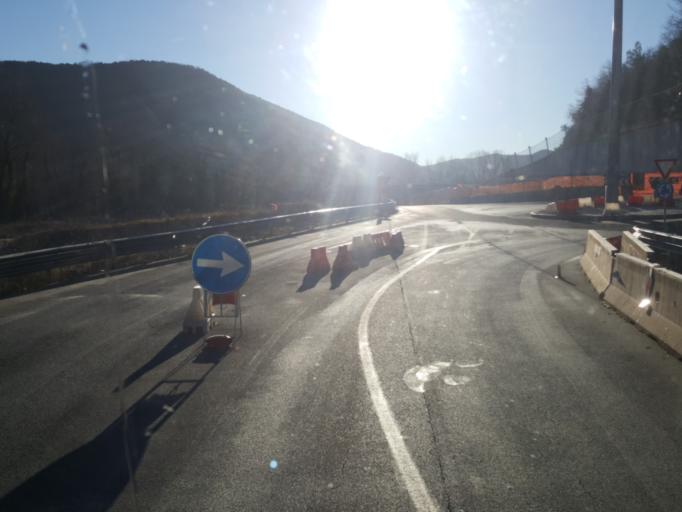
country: IT
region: Latium
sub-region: Provincia di Rieti
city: Colli sul Velino
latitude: 42.5266
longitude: 12.7318
